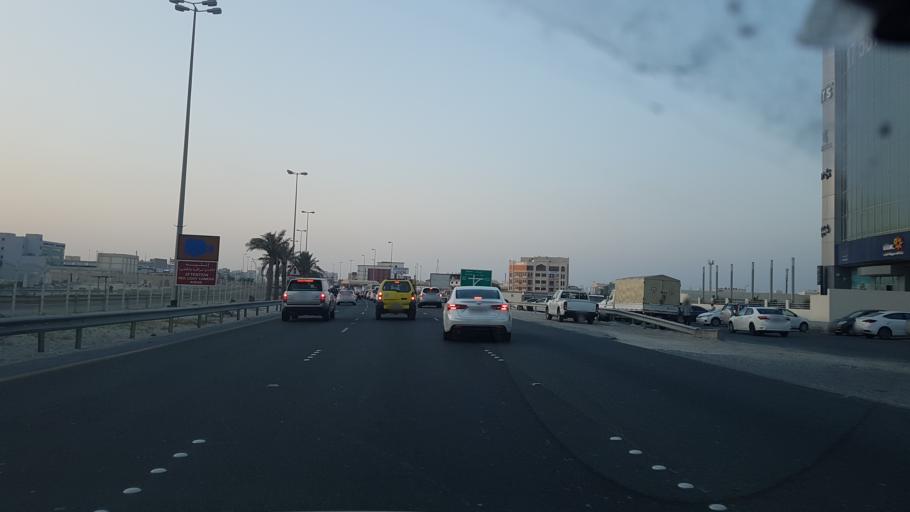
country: BH
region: Northern
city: Ar Rifa'
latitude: 26.1379
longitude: 50.5832
